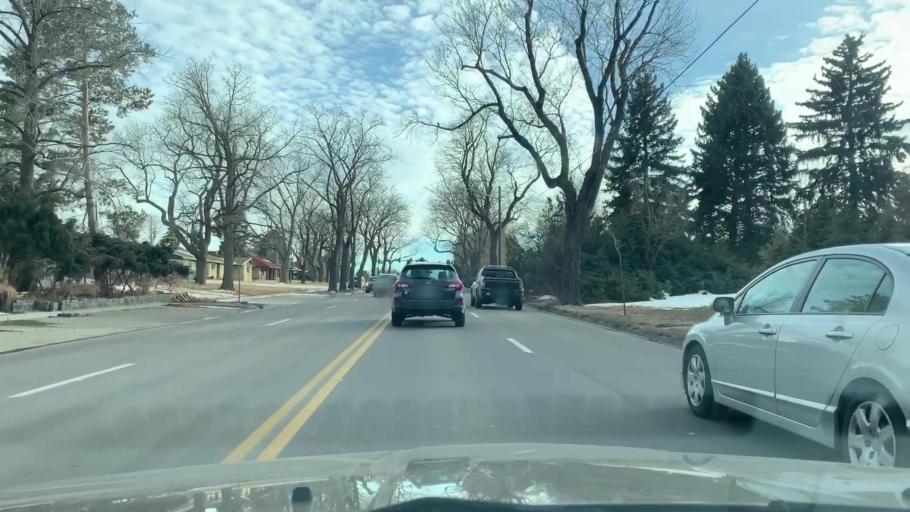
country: US
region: Colorado
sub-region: Arapahoe County
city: Glendale
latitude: 39.7202
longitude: -104.9128
